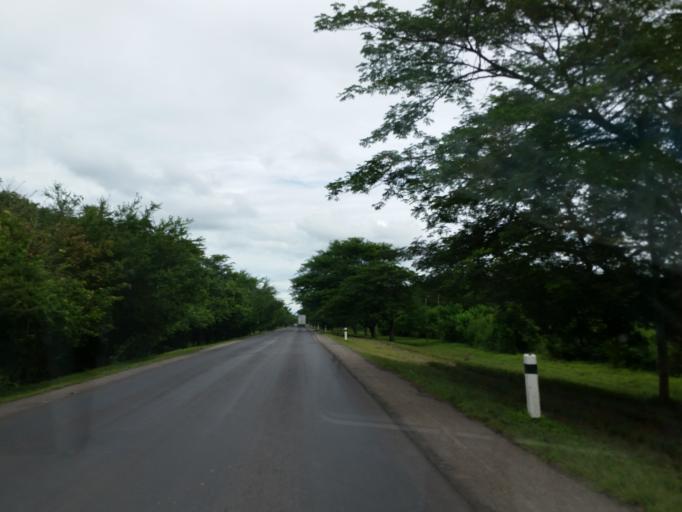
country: NI
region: Chinandega
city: Somotillo
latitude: 12.8460
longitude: -86.8783
